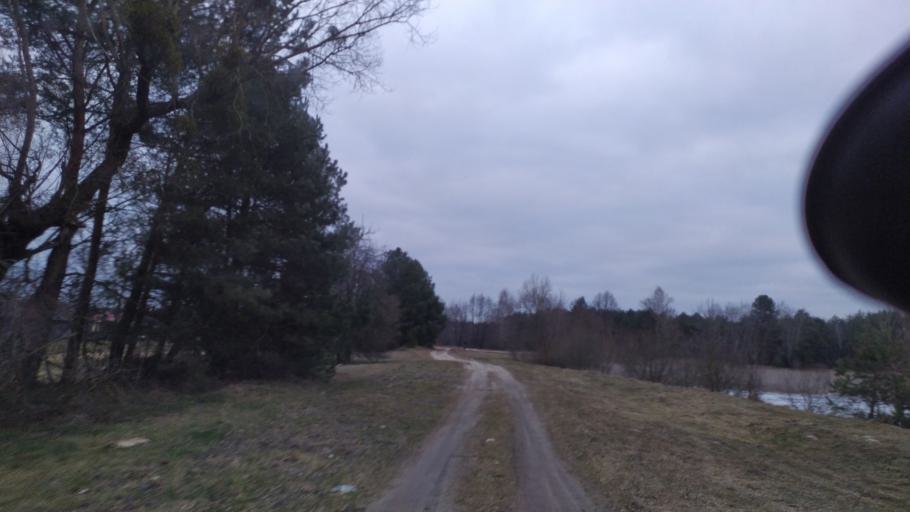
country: PL
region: Lublin Voivodeship
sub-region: Powiat lubartowski
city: Abramow
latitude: 51.4246
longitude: 22.2882
